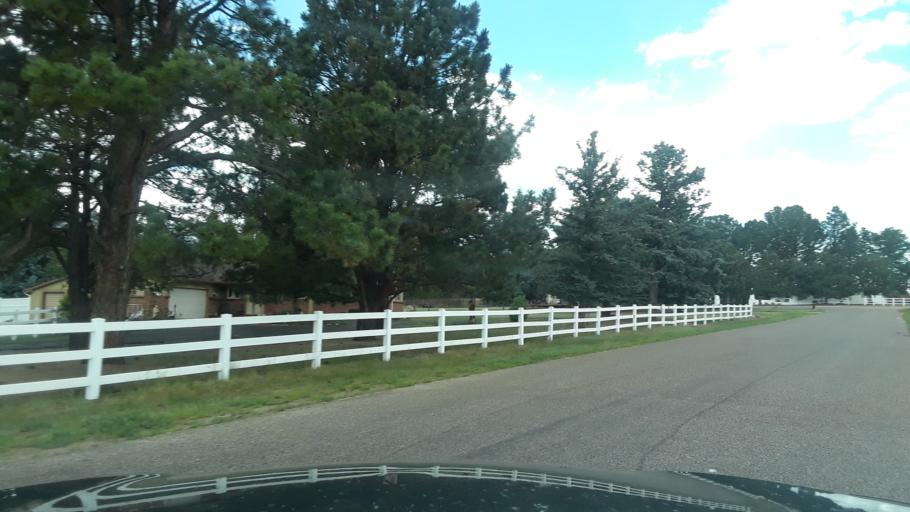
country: US
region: Colorado
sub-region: El Paso County
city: Air Force Academy
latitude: 38.9450
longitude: -104.8202
